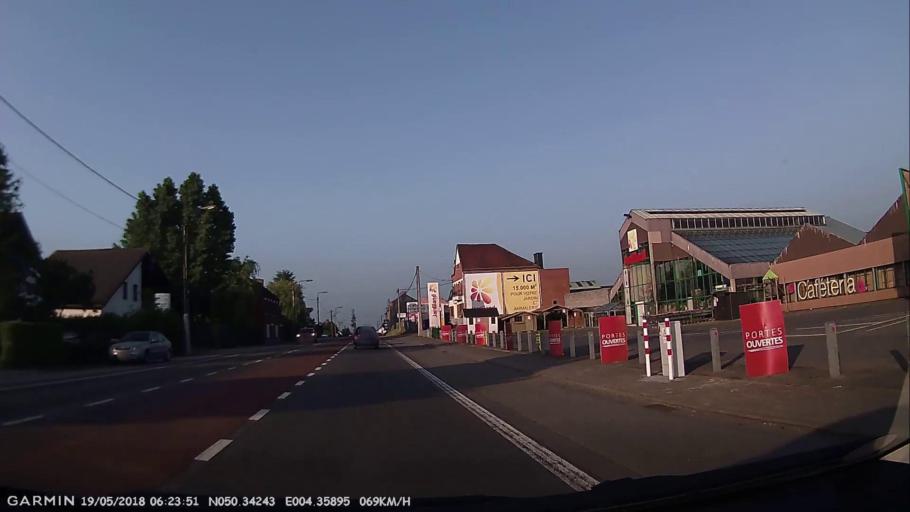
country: BE
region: Wallonia
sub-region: Province du Hainaut
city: Thuin
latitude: 50.3424
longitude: 4.3589
